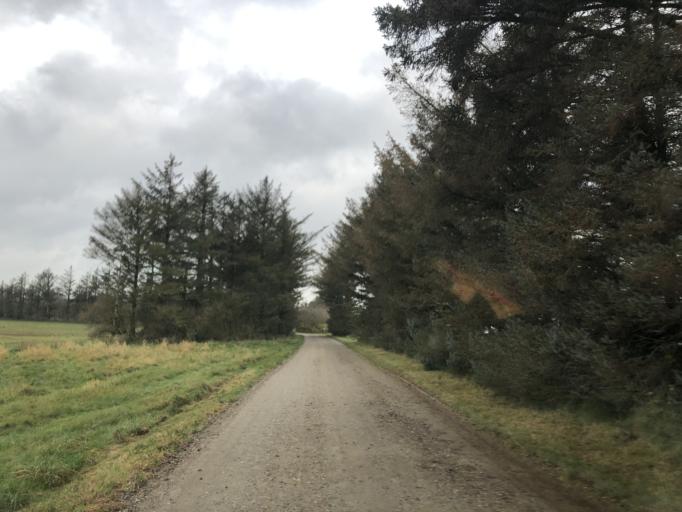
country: DK
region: Central Jutland
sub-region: Holstebro Kommune
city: Ulfborg
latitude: 56.3202
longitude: 8.2267
